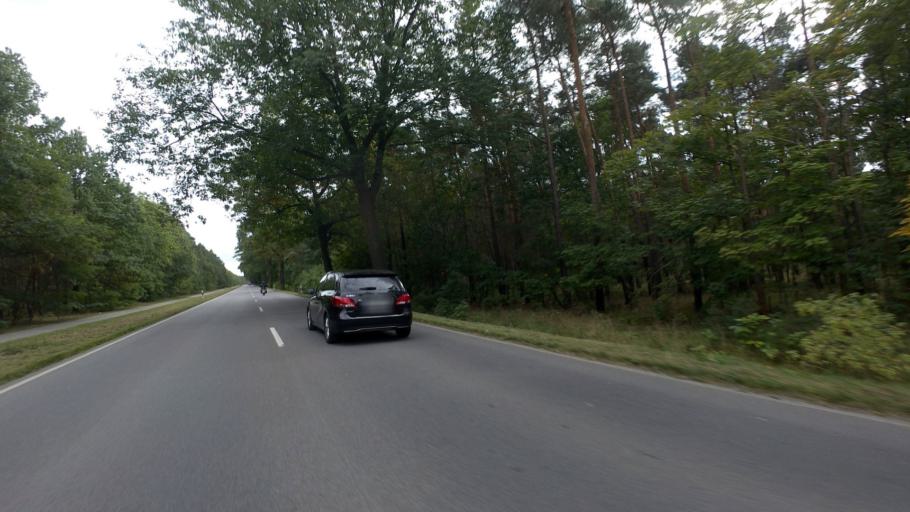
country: DE
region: Saxony
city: Wittichenau
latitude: 51.4167
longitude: 14.2834
